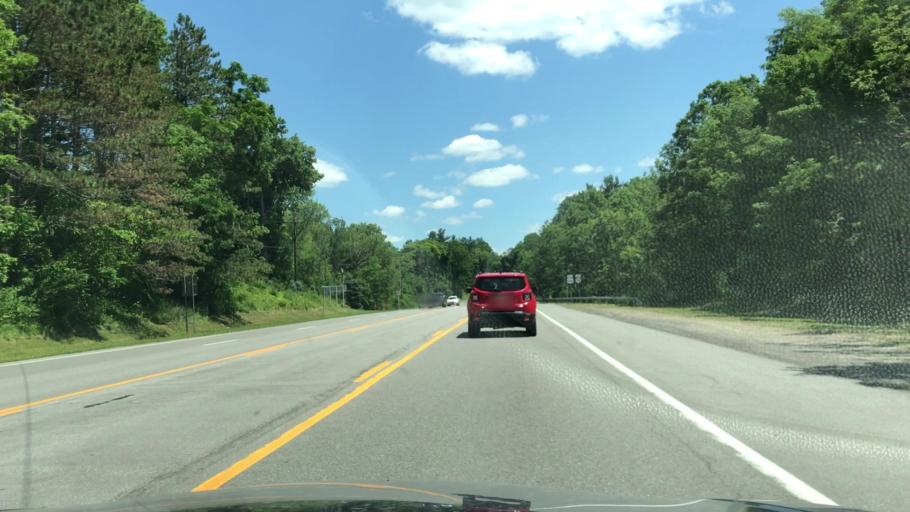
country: US
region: New York
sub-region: Erie County
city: East Aurora
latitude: 42.7675
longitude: -78.5919
